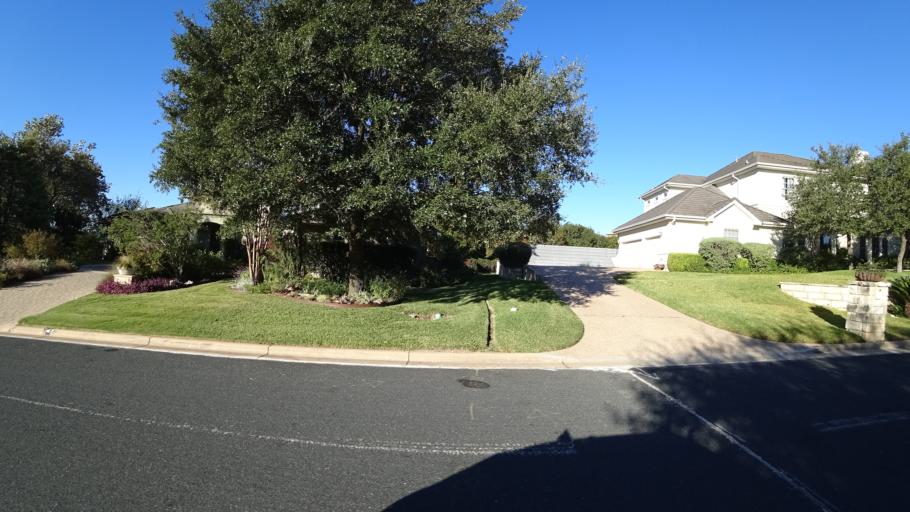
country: US
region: Texas
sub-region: Travis County
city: West Lake Hills
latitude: 30.3204
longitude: -97.8102
